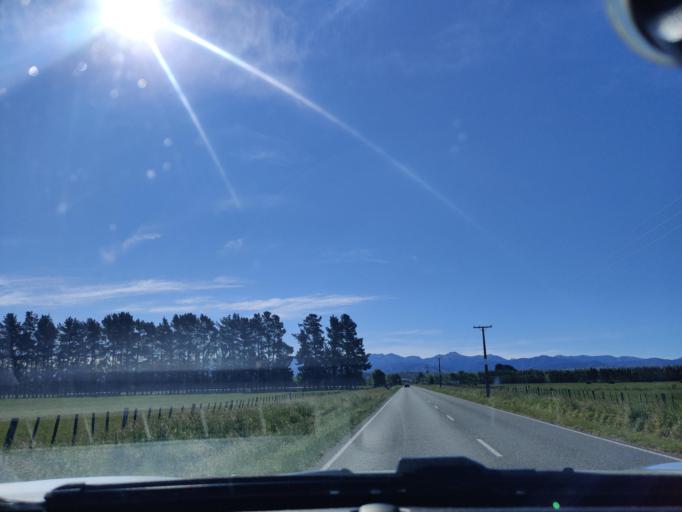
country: NZ
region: Wellington
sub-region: Masterton District
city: Masterton
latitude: -40.9349
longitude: 175.6495
